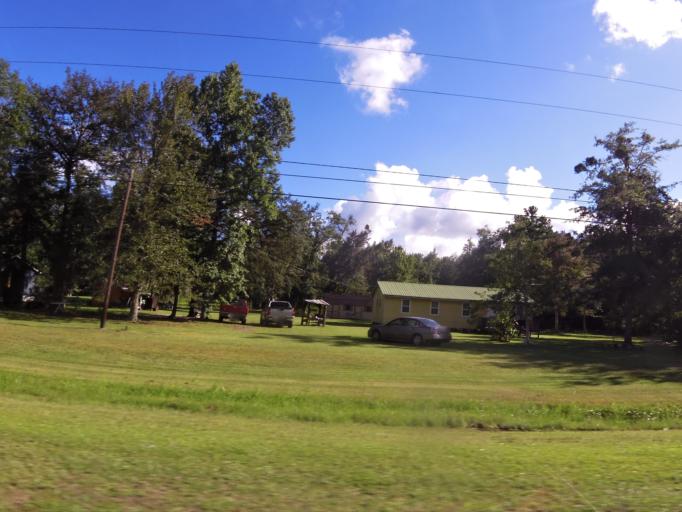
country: US
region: Georgia
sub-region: Camden County
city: Woodbine
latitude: 31.1067
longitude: -81.6539
